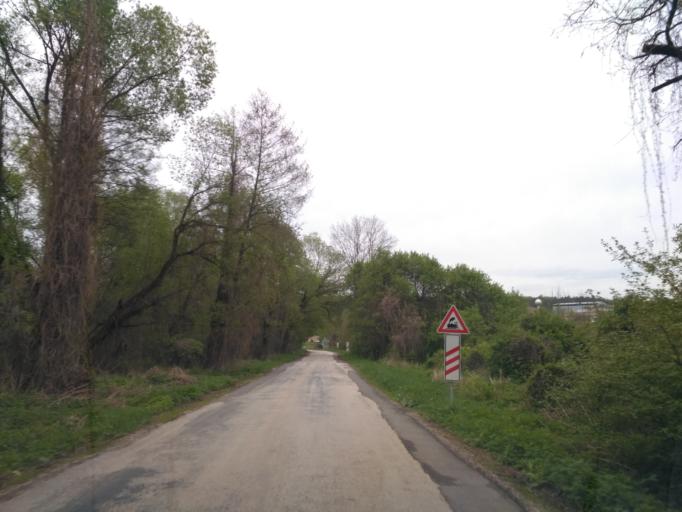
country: SK
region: Kosicky
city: Moldava nad Bodvou
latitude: 48.6484
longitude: 21.0037
